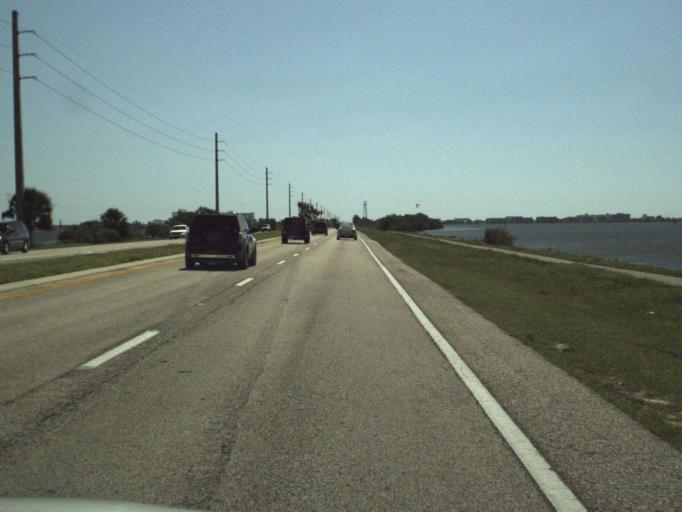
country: US
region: Florida
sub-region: Brevard County
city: Cocoa Beach
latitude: 28.3576
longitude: -80.6403
